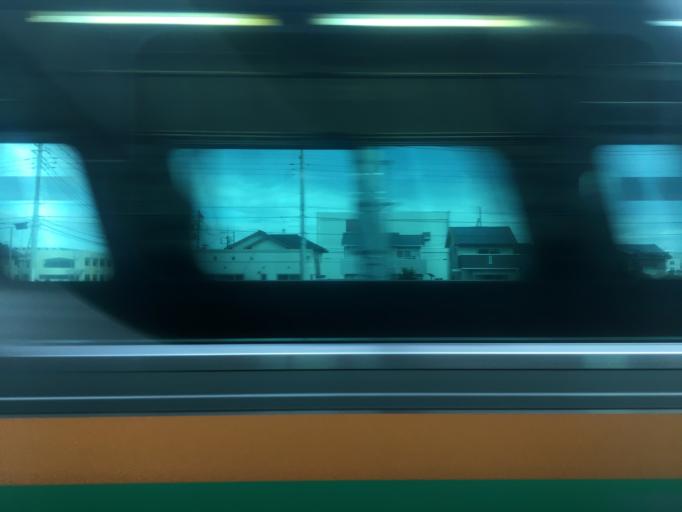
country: JP
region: Saitama
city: Konosu
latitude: 36.0778
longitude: 139.4867
